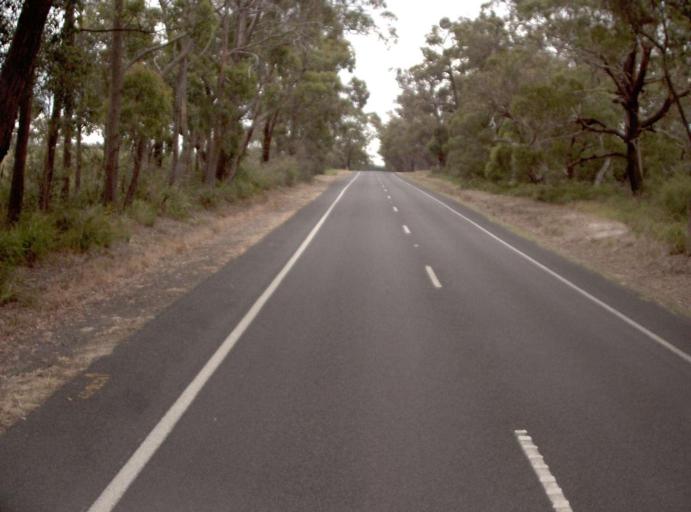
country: AU
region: Victoria
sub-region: Wellington
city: Sale
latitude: -38.2309
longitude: 147.0547
